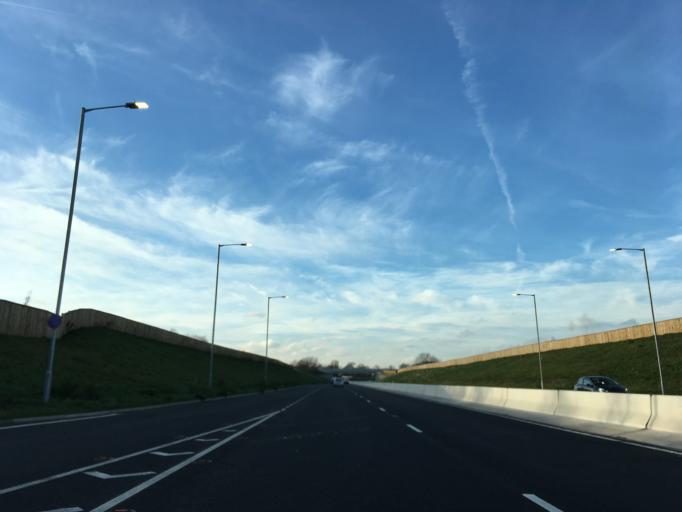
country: GB
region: England
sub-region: Cheshire East
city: Wilmslow
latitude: 53.3563
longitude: -2.2242
